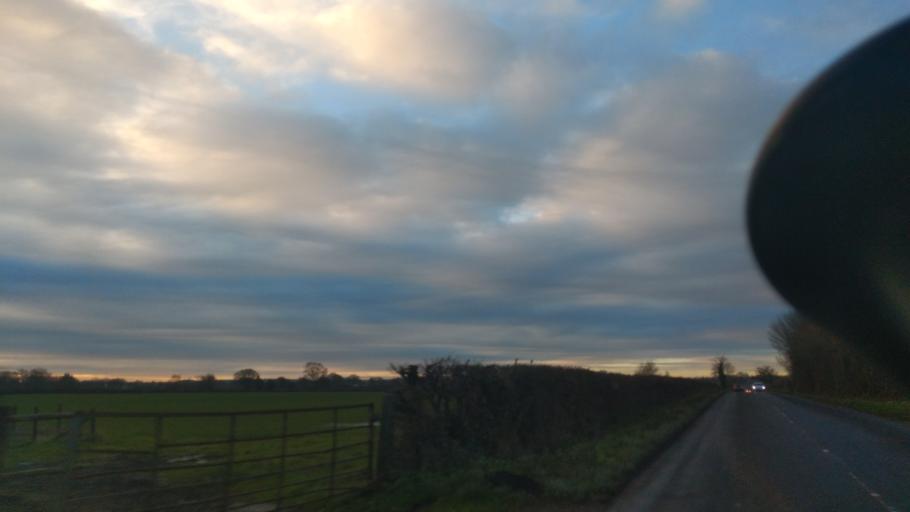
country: GB
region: England
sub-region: Wiltshire
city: Wingfield
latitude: 51.3000
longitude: -2.2610
